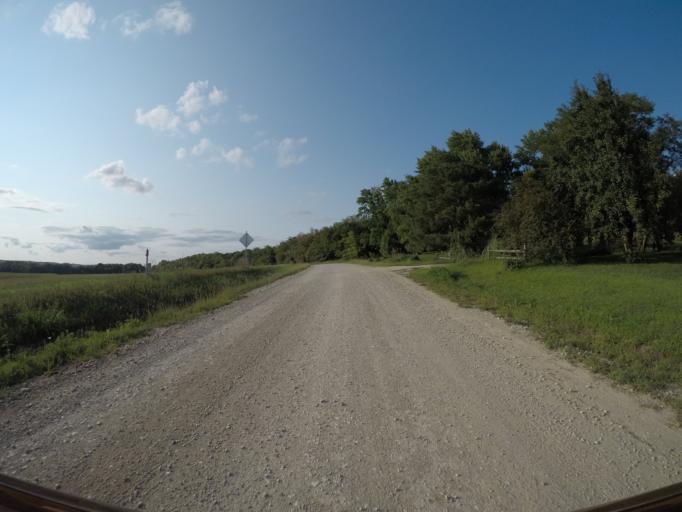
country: US
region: Kansas
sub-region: Wabaunsee County
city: Alma
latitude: 38.9221
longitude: -96.2222
